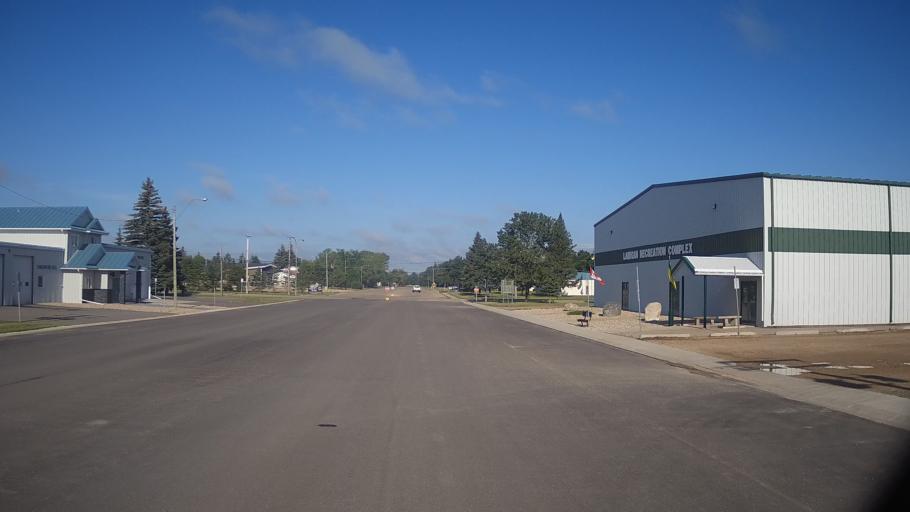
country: CA
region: Saskatchewan
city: Lanigan
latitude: 51.8509
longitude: -105.0293
